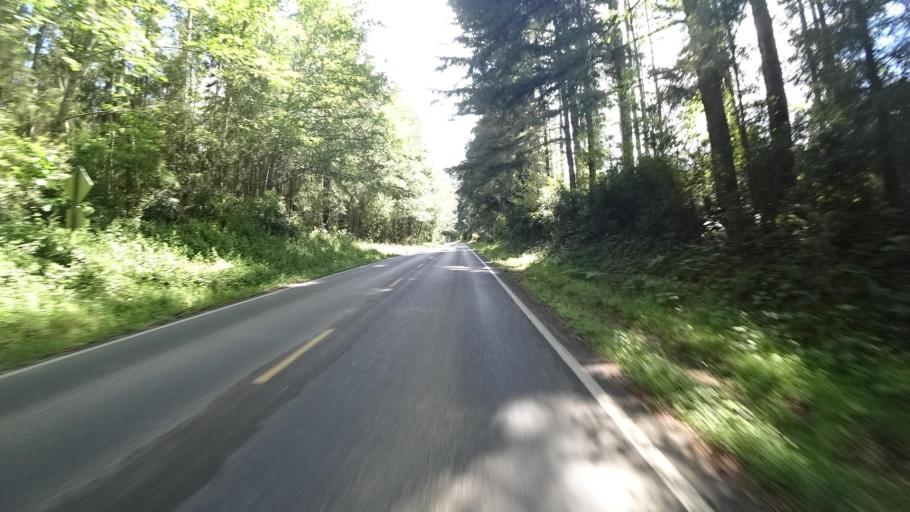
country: US
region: California
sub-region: Humboldt County
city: McKinleyville
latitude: 40.9552
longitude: -124.0752
